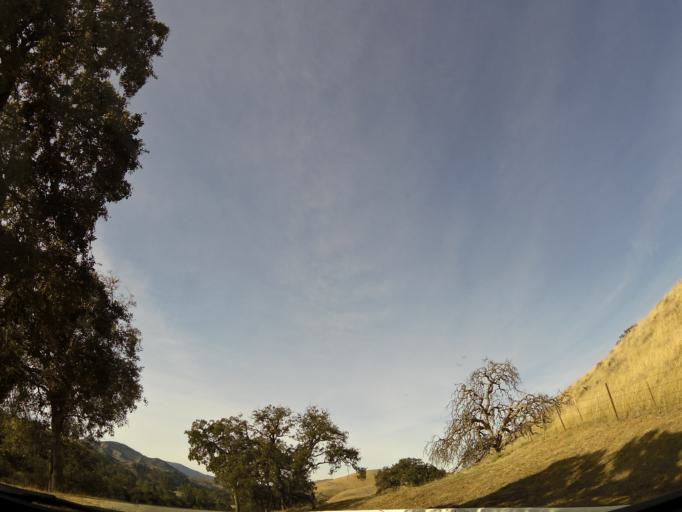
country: US
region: California
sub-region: San Benito County
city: Ridgemark
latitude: 36.6876
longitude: -121.2991
